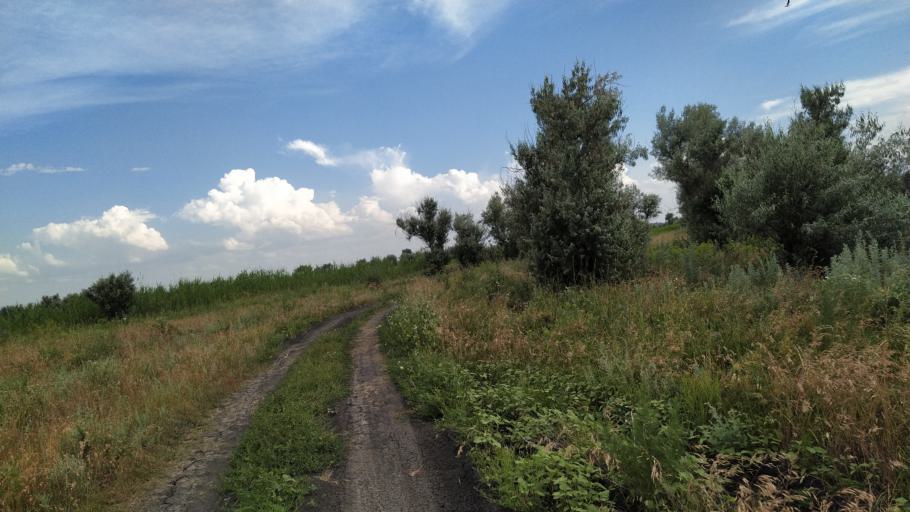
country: RU
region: Rostov
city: Kuleshovka
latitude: 47.1372
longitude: 39.6337
